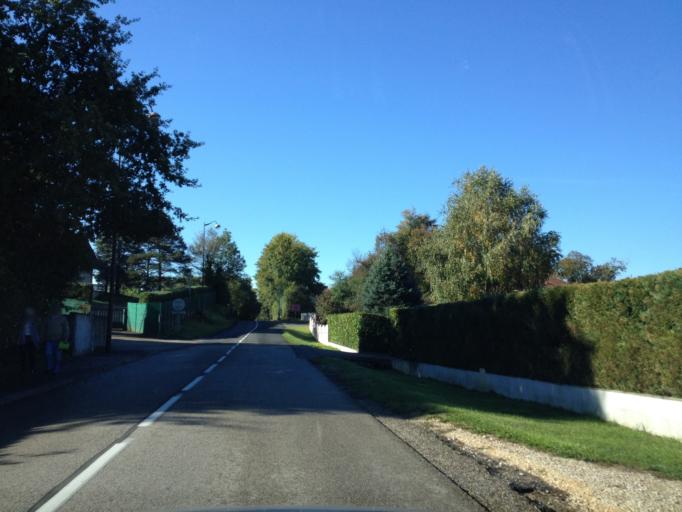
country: FR
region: Rhone-Alpes
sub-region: Departement de l'Isere
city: Morestel
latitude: 45.6689
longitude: 5.4662
